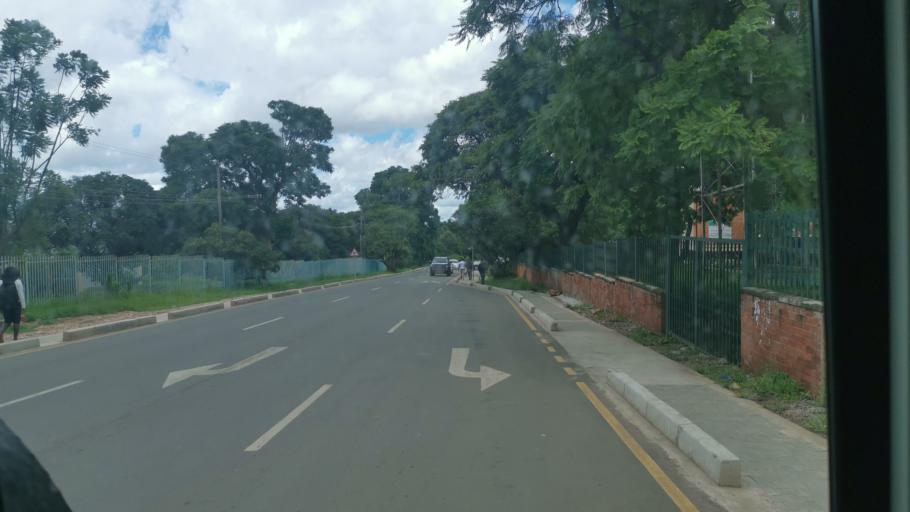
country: ZM
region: Lusaka
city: Lusaka
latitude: -15.4270
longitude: 28.3117
